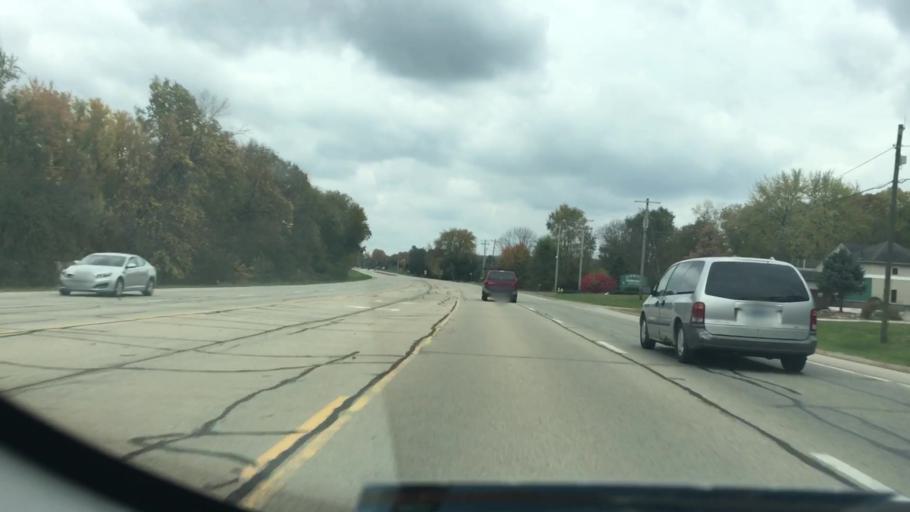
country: US
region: Illinois
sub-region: Peoria County
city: Peoria Heights
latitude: 40.7771
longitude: -89.5765
